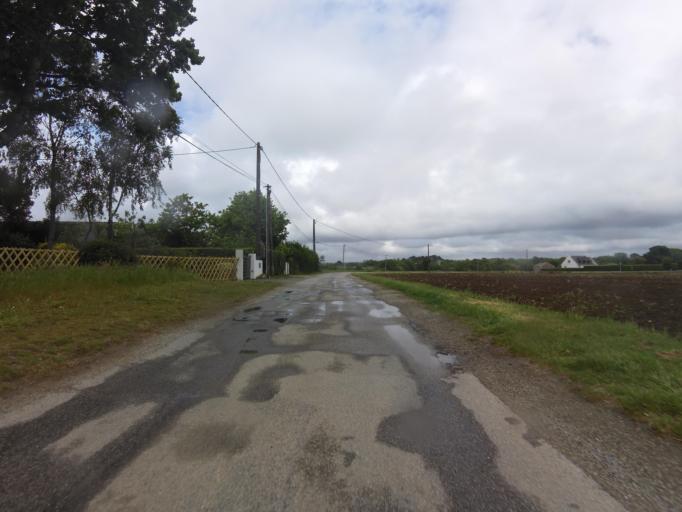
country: FR
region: Brittany
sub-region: Departement du Morbihan
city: Plougoumelen
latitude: 47.6355
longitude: -2.9145
